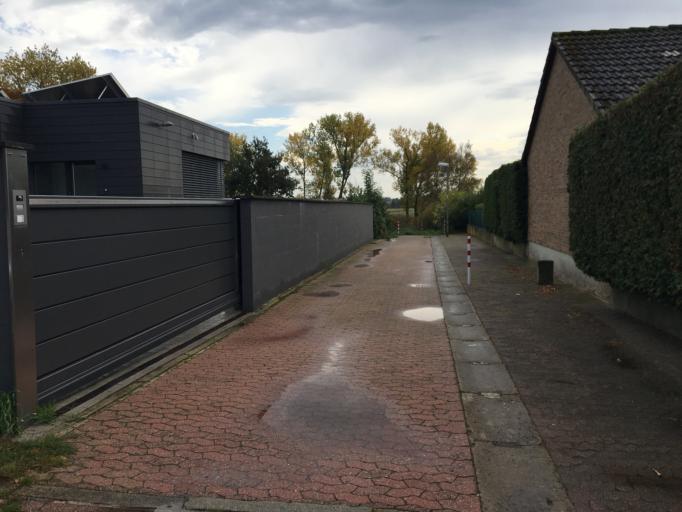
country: DE
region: Lower Saxony
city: Braunschweig
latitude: 52.3021
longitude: 10.5738
